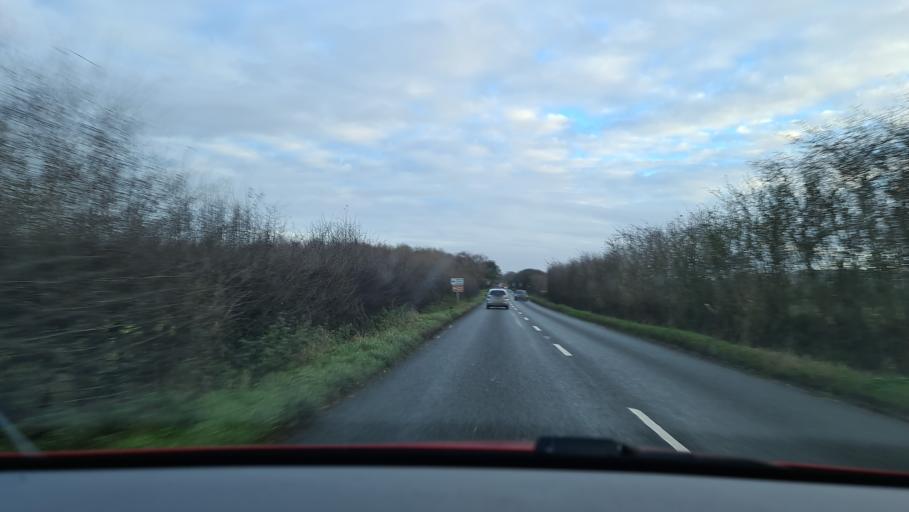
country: GB
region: England
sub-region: Buckinghamshire
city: Princes Risborough
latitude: 51.7416
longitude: -0.8340
